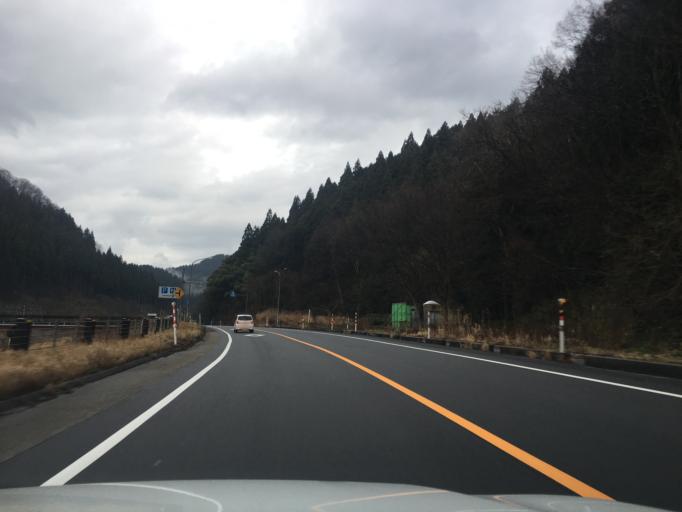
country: JP
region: Niigata
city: Murakami
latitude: 38.4697
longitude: 139.5561
